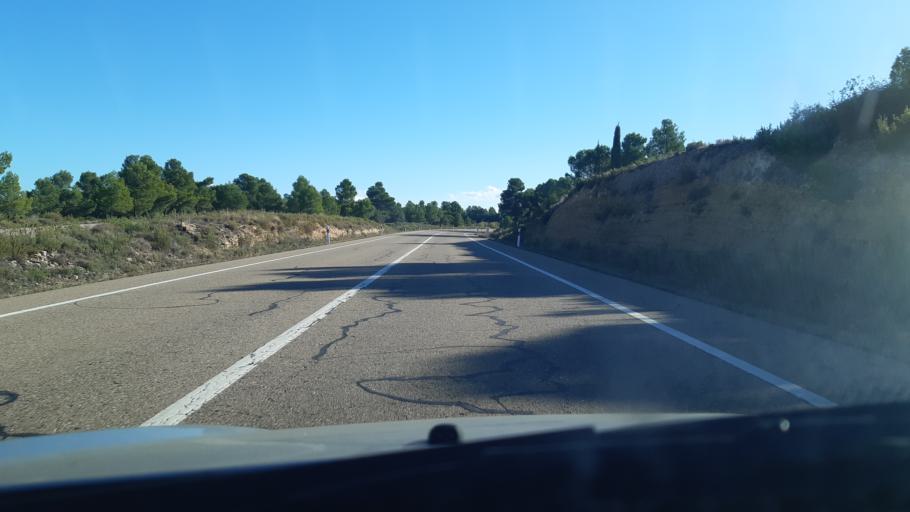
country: ES
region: Aragon
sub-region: Provincia de Teruel
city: Valjunquera
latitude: 40.9408
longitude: -0.0118
